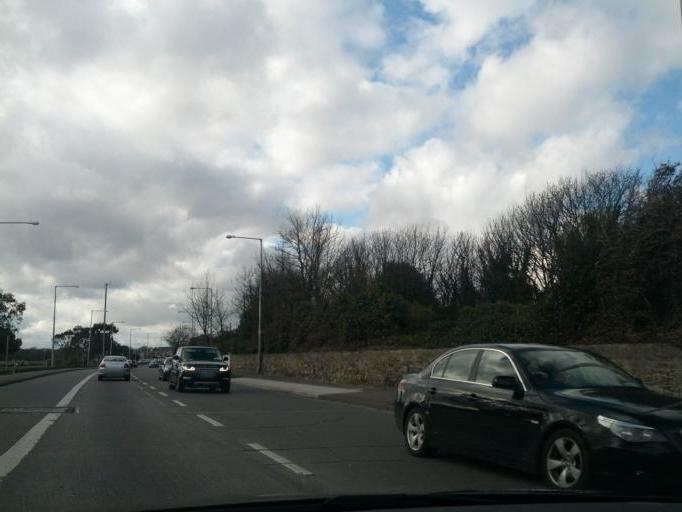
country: IE
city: Donnycarney
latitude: 53.3606
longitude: -6.2124
